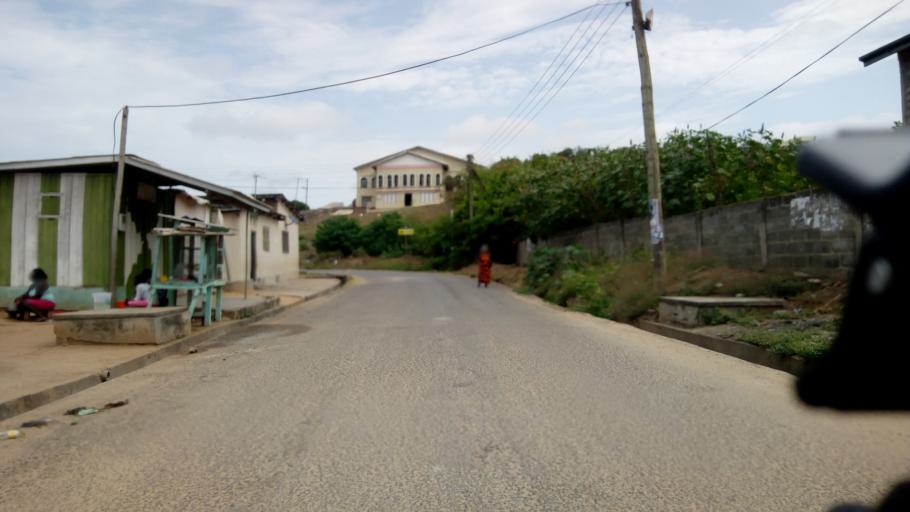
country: GH
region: Central
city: Cape Coast
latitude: 5.1019
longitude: -1.2755
